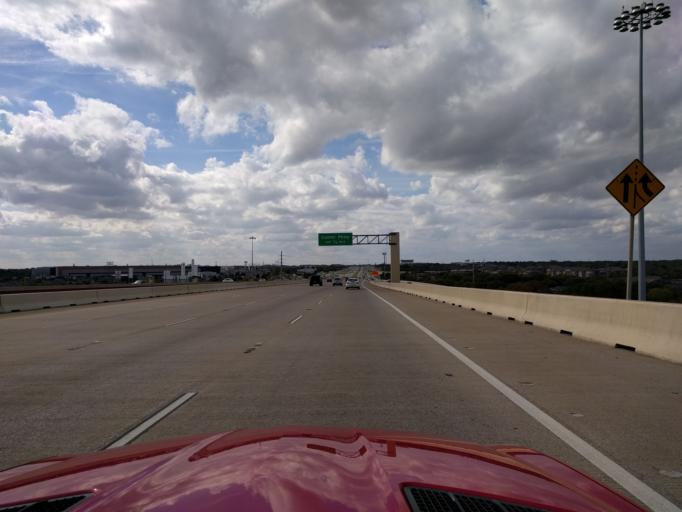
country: US
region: Texas
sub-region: Collin County
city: Plano
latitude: 33.0041
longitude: -96.7103
